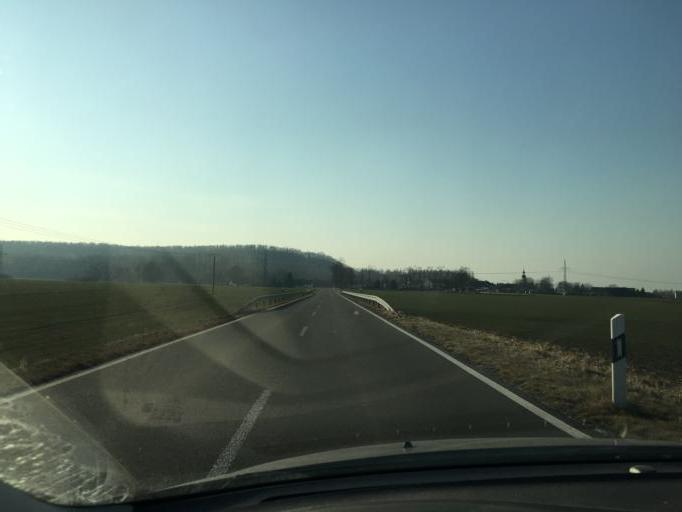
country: DE
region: Saxony
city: Kitzscher
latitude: 51.1894
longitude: 12.5376
